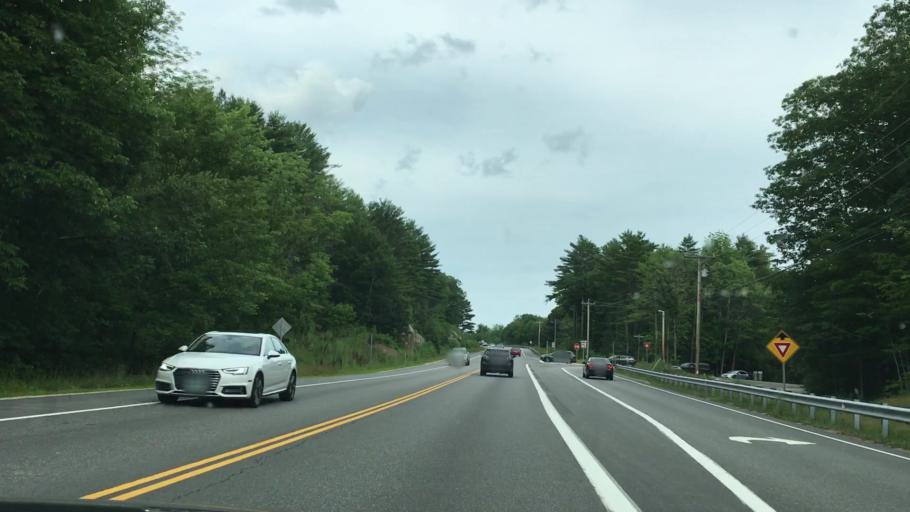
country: US
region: New Hampshire
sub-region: Belknap County
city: Meredith
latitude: 43.6231
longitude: -71.5531
